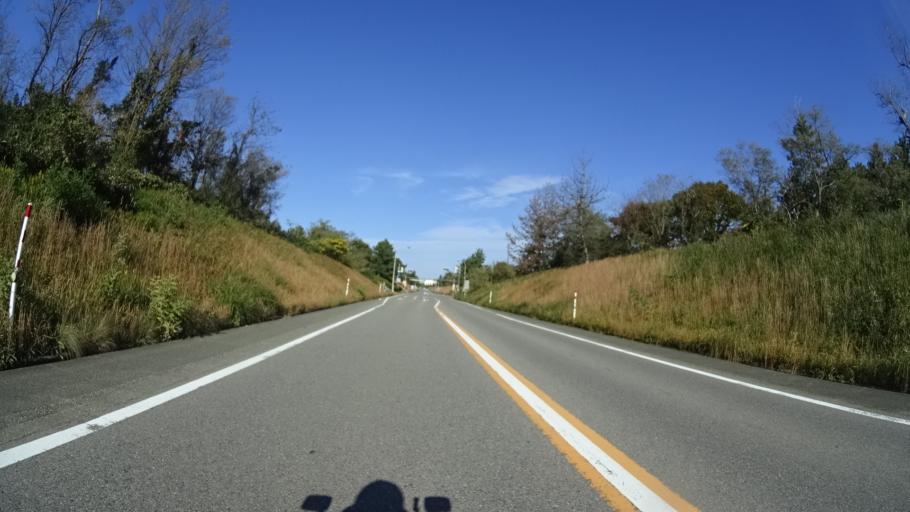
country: JP
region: Ishikawa
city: Kanazawa-shi
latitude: 36.6394
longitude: 136.6314
